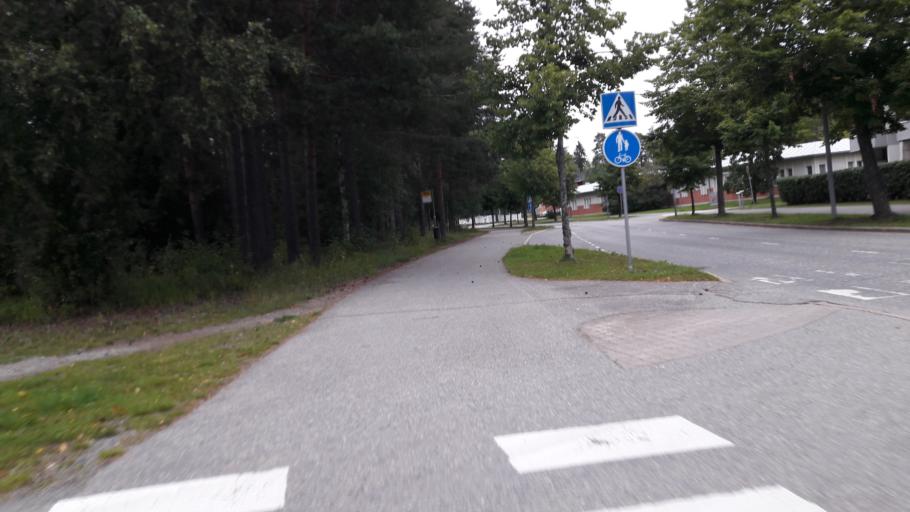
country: FI
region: North Karelia
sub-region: Joensuu
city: Joensuu
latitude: 62.6187
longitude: 29.7087
